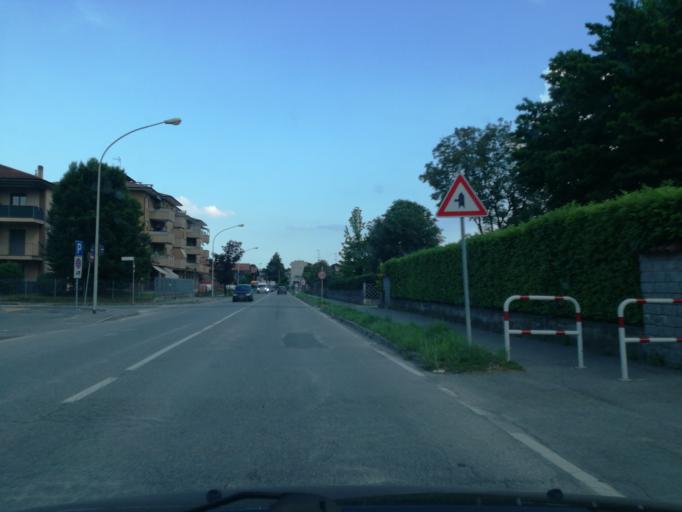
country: IT
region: Lombardy
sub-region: Provincia di Monza e Brianza
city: Porto d'Adda
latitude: 45.6481
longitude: 9.4633
